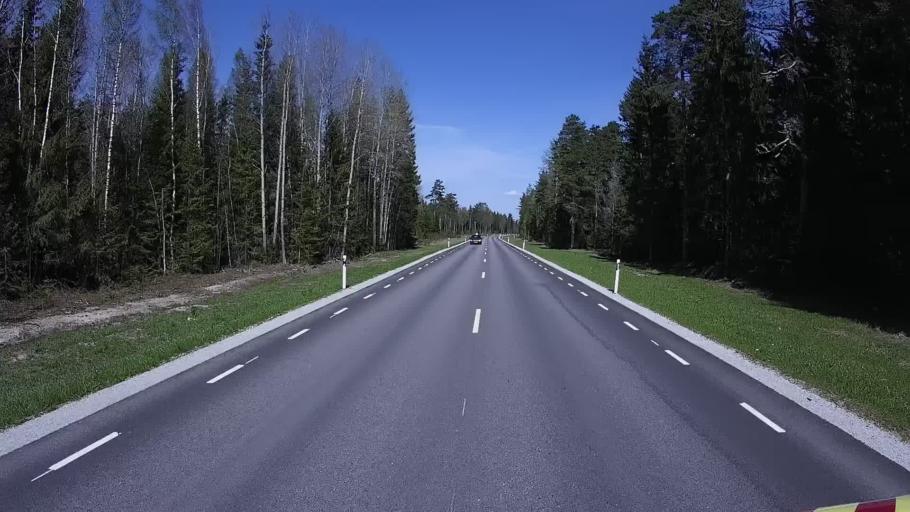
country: EE
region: Harju
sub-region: Nissi vald
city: Turba
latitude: 59.1372
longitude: 24.0758
